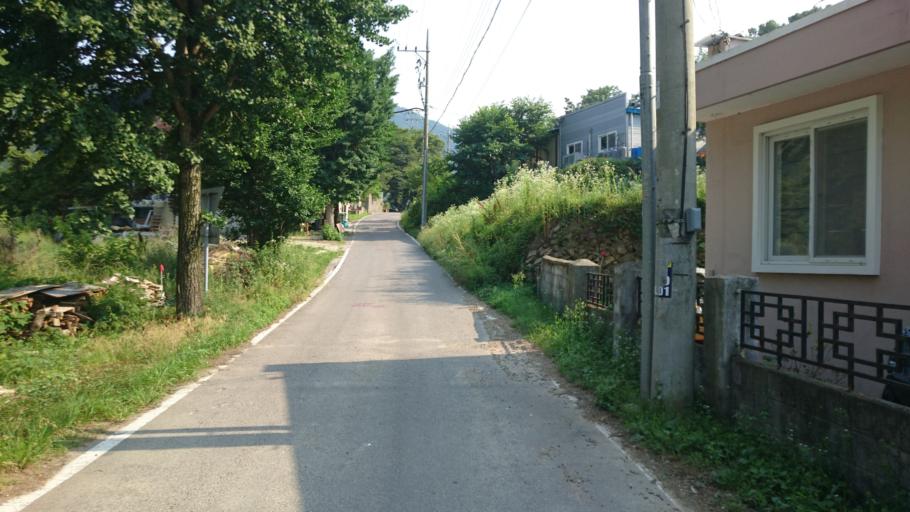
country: KR
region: Gyeongsangbuk-do
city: Gyeongsan-si
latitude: 35.7343
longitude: 128.6595
